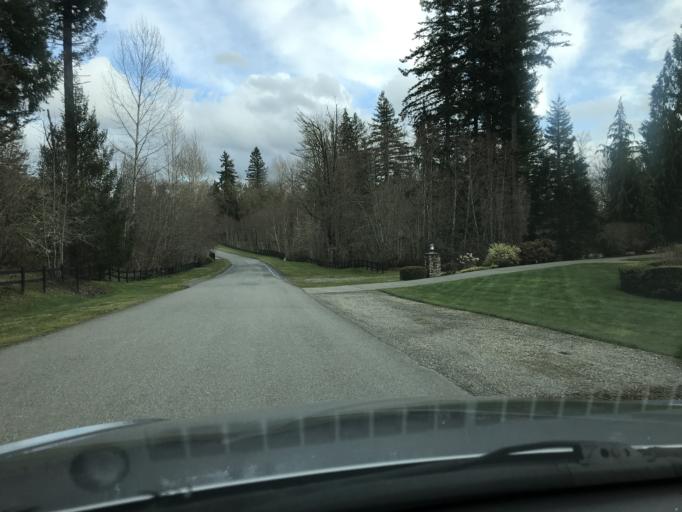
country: US
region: Washington
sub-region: King County
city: Union Hill-Novelty Hill
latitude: 47.6573
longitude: -122.0093
